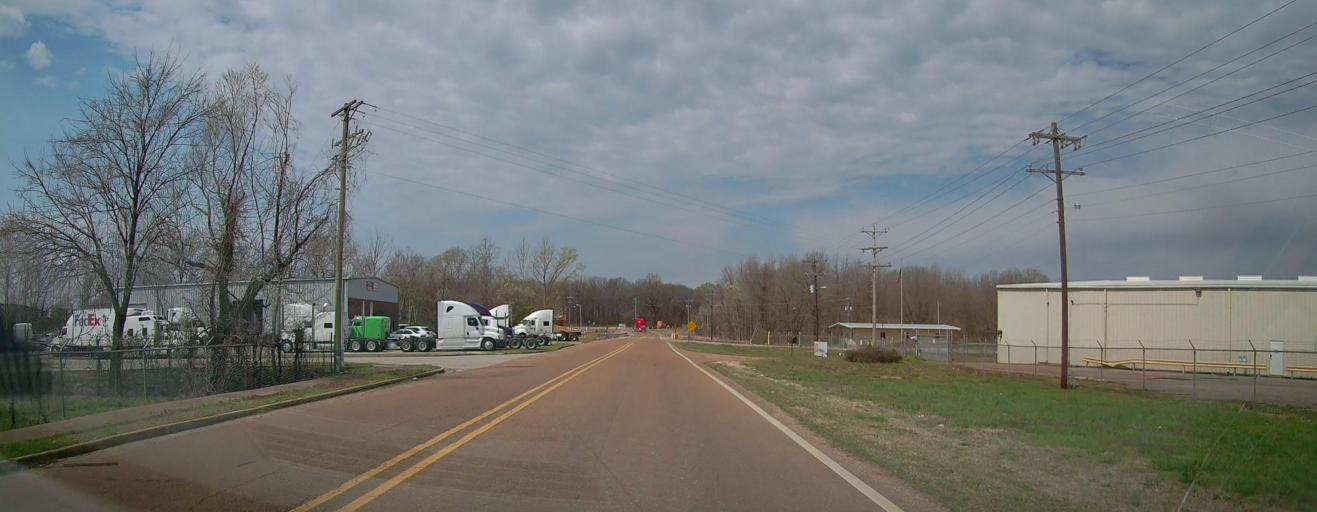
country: US
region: Mississippi
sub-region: De Soto County
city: Olive Branch
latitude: 34.9913
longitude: -89.8639
